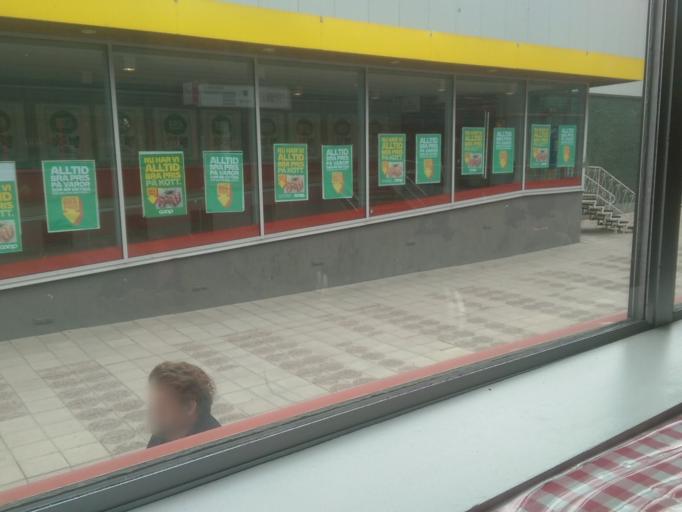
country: SE
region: Dalarna
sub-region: Avesta Kommun
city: Avesta
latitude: 60.1460
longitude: 16.1717
